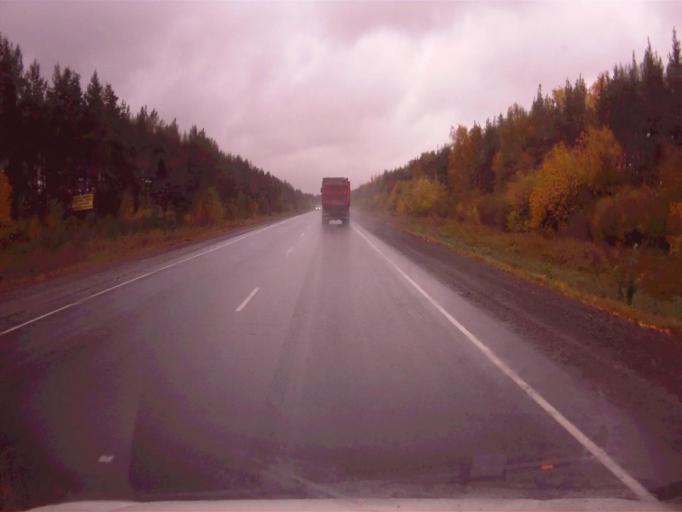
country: RU
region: Chelyabinsk
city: Roshchino
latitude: 55.3566
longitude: 61.2500
